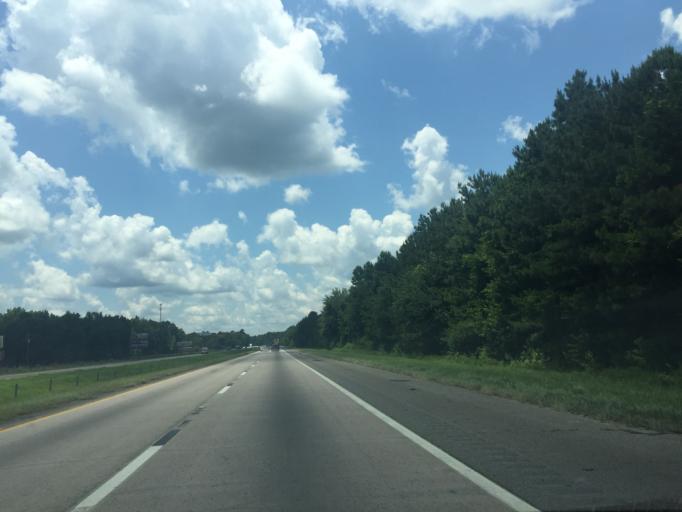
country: US
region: South Carolina
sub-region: Jasper County
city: Ridgeland
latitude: 32.4581
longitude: -80.9845
